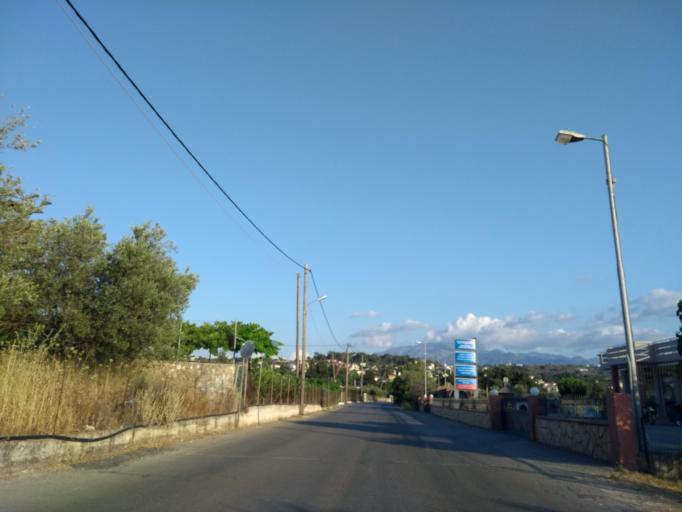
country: GR
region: Crete
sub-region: Nomos Chanias
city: Kalivai
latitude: 35.4144
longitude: 24.1945
